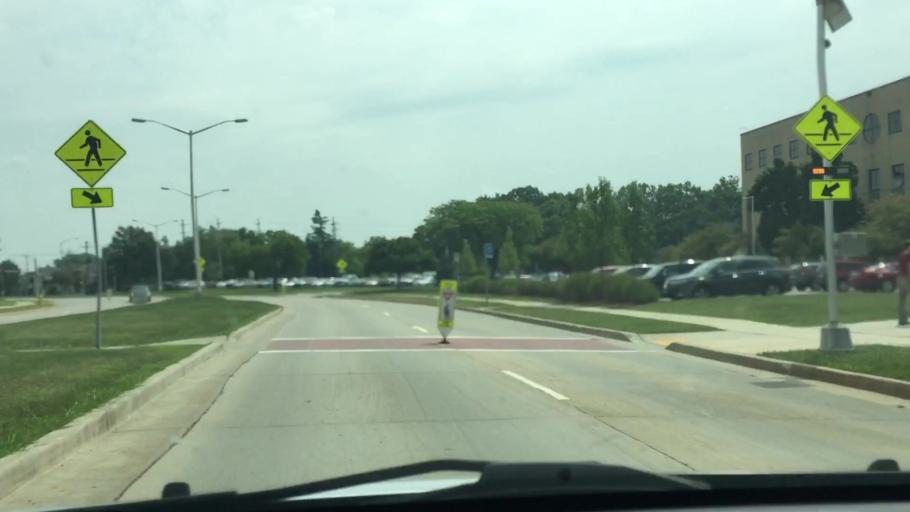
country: US
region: Wisconsin
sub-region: Waukesha County
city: Waukesha
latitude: 43.0236
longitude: -88.2287
